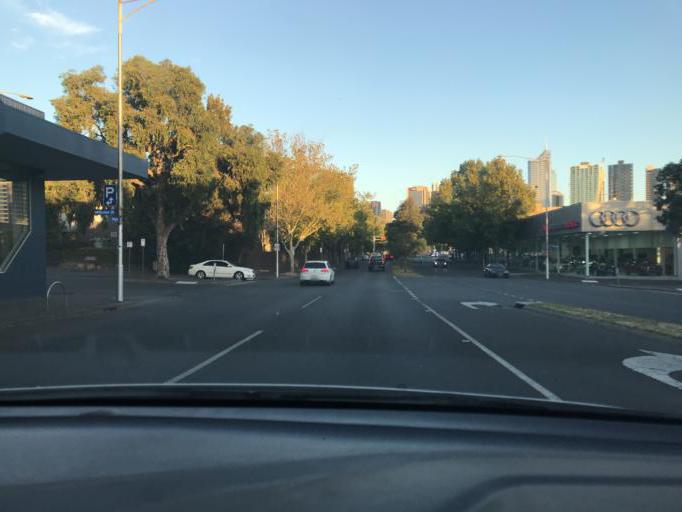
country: AU
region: Victoria
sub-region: Melbourne
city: North Melbourne
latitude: -37.8058
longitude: 144.9493
